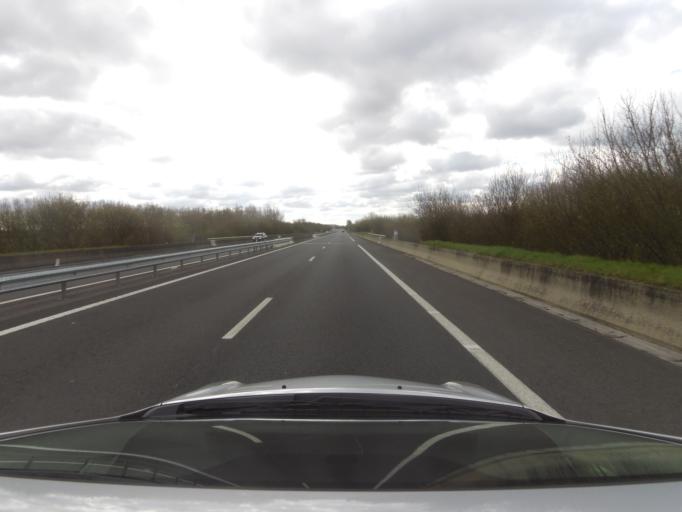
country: FR
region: Picardie
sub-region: Departement de la Somme
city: Quend
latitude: 50.3455
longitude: 1.6920
